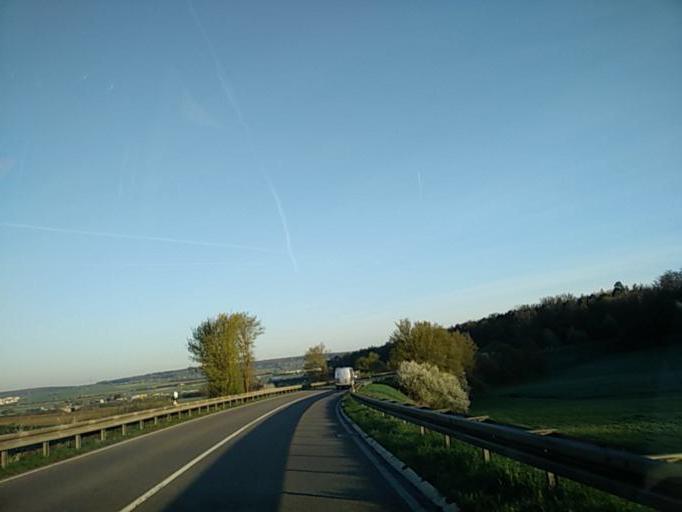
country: DE
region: Baden-Wuerttemberg
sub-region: Regierungsbezirk Stuttgart
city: Ehningen
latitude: 48.6397
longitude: 8.9440
